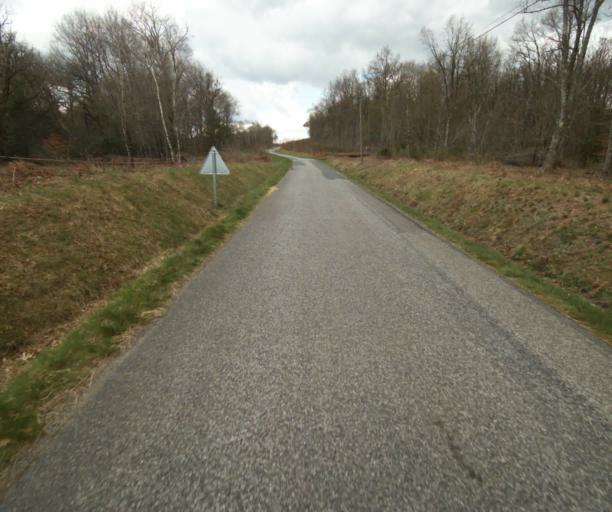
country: FR
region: Limousin
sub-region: Departement de la Correze
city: Correze
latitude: 45.2640
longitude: 1.9043
